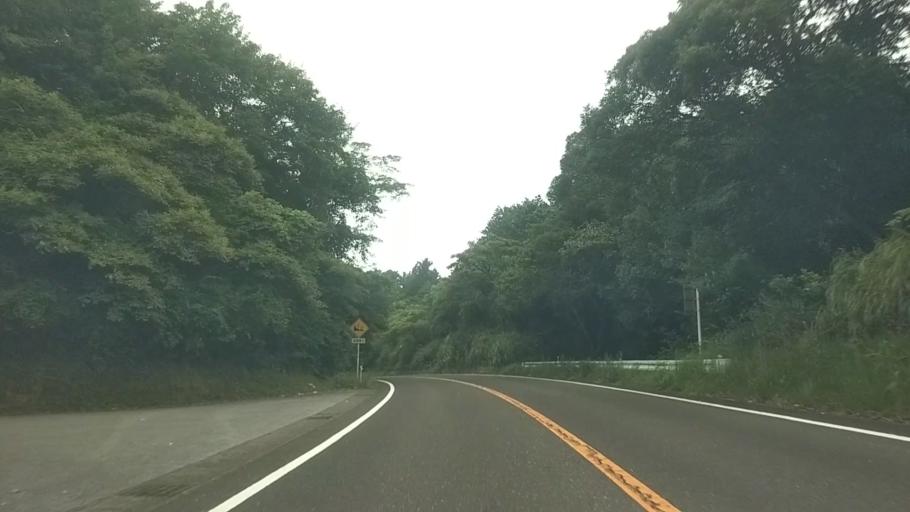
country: JP
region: Chiba
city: Kawaguchi
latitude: 35.2162
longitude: 140.0461
